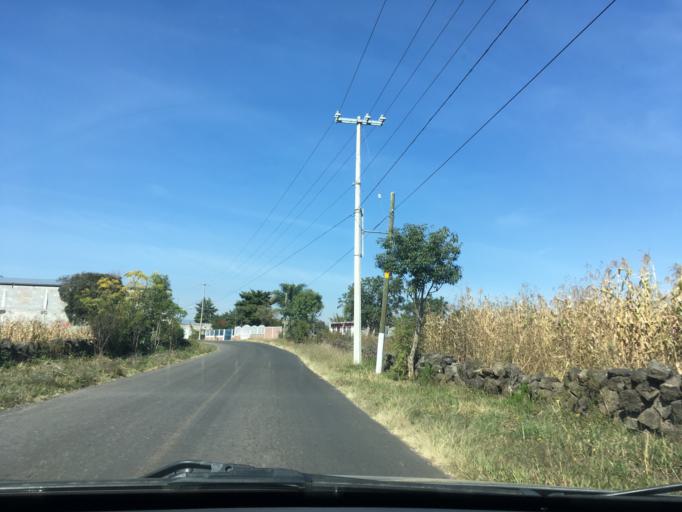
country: MX
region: Michoacan
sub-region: Morelia
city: La Mintzita (Piedra Dura)
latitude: 19.6506
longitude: -101.3054
